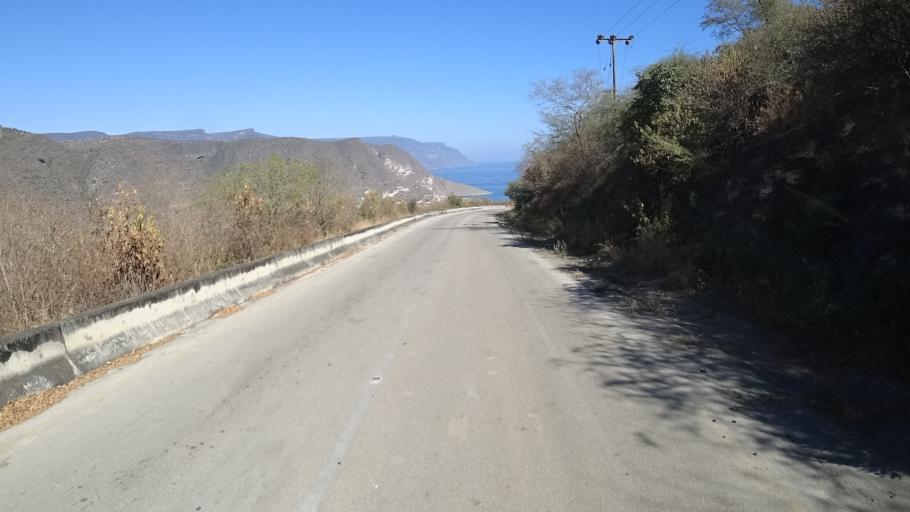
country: YE
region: Al Mahrah
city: Hawf
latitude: 16.7459
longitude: 53.4059
